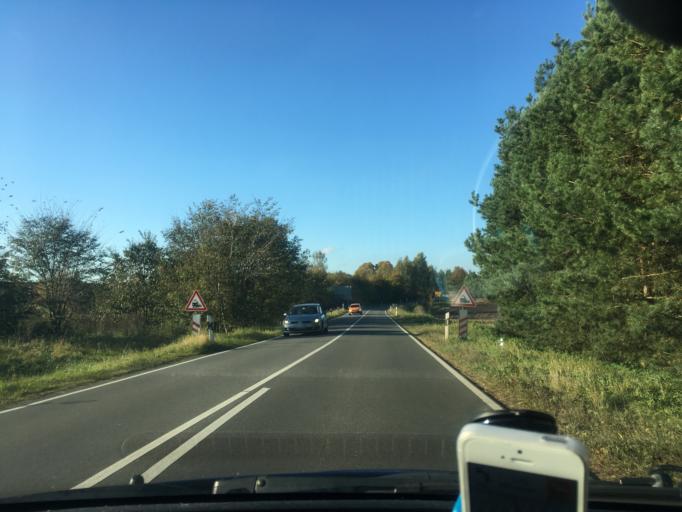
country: DE
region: Mecklenburg-Vorpommern
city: Zarrentin
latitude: 53.5416
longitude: 10.9315
